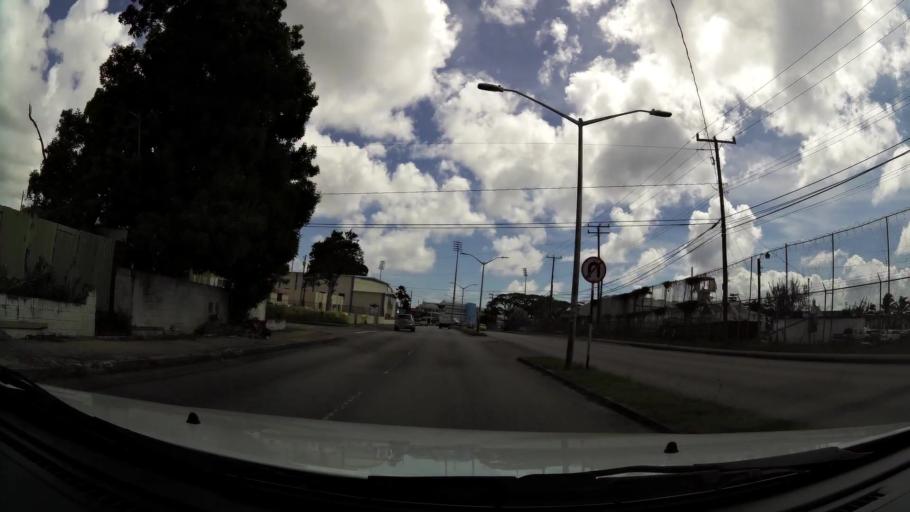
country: BB
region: Saint Michael
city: Bridgetown
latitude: 13.1076
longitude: -59.6251
